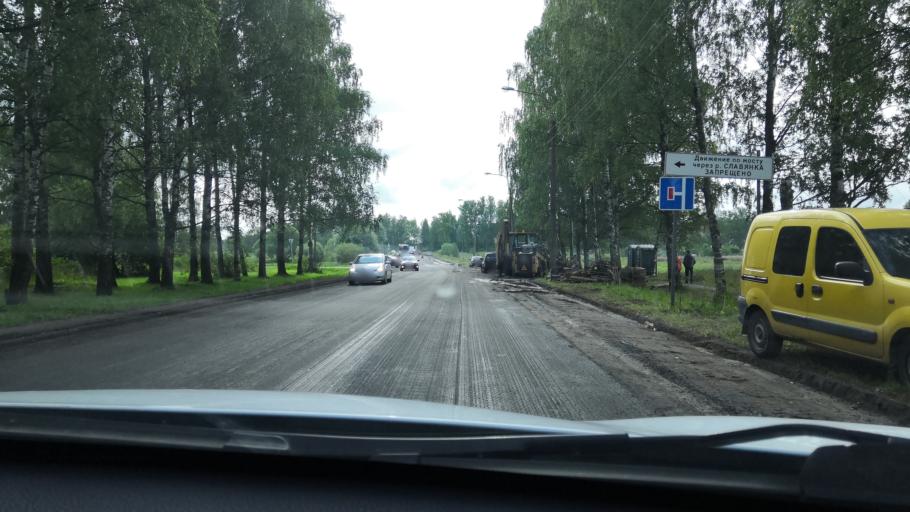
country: RU
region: St.-Petersburg
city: Tyarlevo
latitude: 59.7121
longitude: 30.4651
